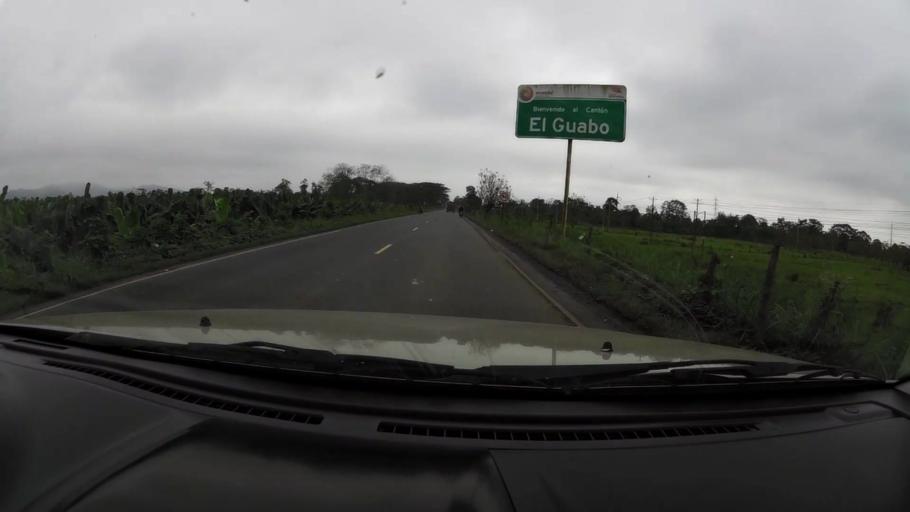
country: EC
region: Guayas
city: Balao
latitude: -3.0810
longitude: -79.7570
